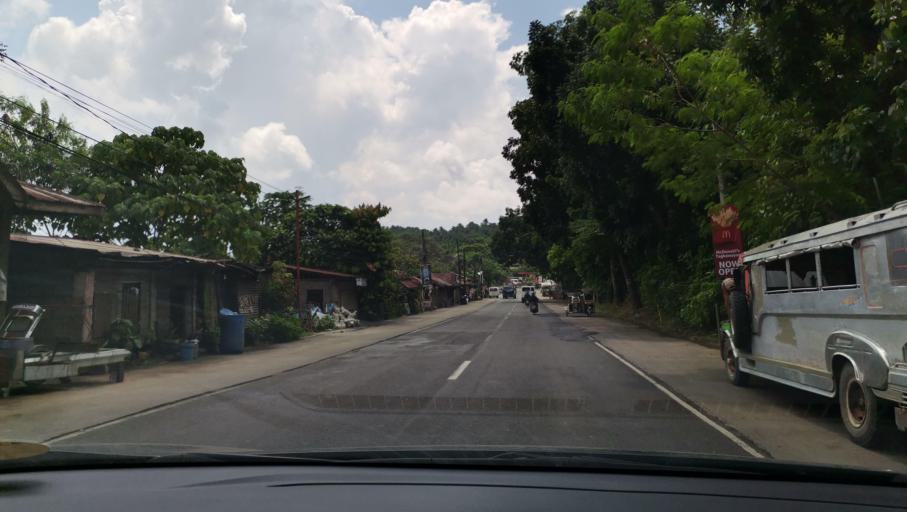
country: PH
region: Calabarzon
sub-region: Province of Quezon
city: Calauag
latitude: 13.9544
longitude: 122.2919
